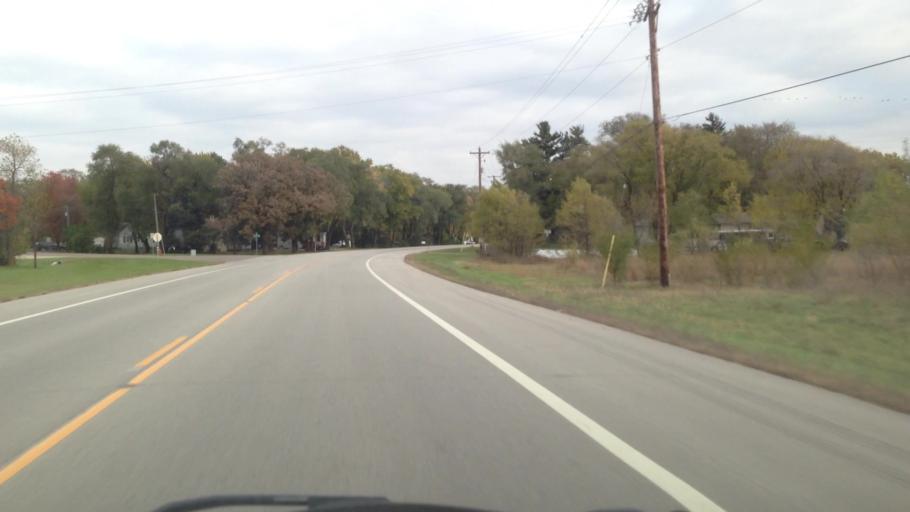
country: US
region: Minnesota
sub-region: Olmsted County
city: Rochester
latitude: 43.9857
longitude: -92.4052
